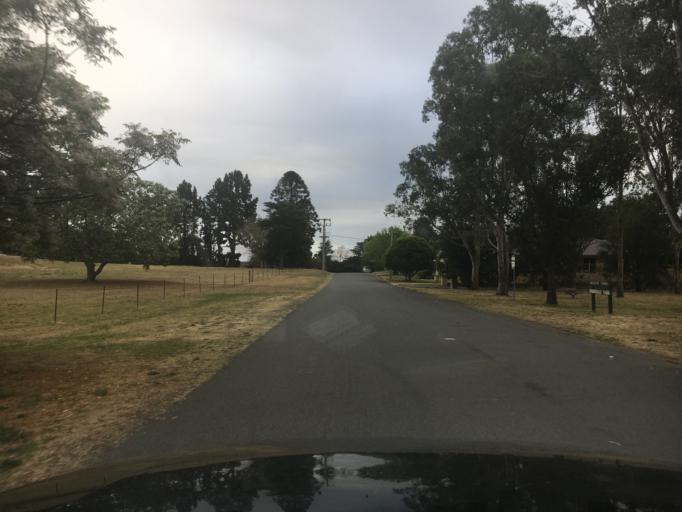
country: AU
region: New South Wales
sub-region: Singleton
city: Singleton
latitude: -32.5684
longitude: 151.1871
